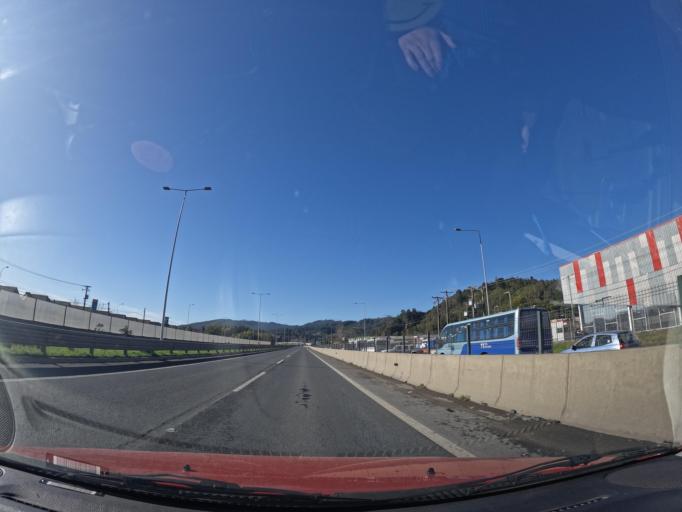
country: CL
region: Biobio
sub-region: Provincia de Concepcion
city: Concepcion
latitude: -36.8204
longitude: -73.0039
